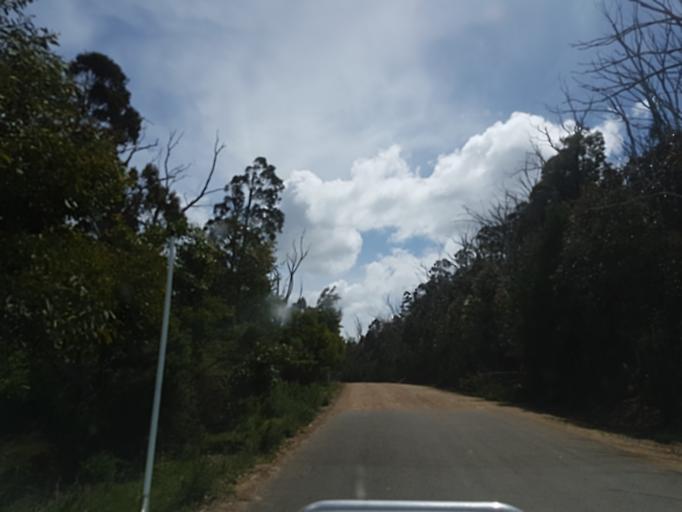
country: AU
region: Victoria
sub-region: Alpine
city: Mount Beauty
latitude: -37.3508
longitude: 147.2067
